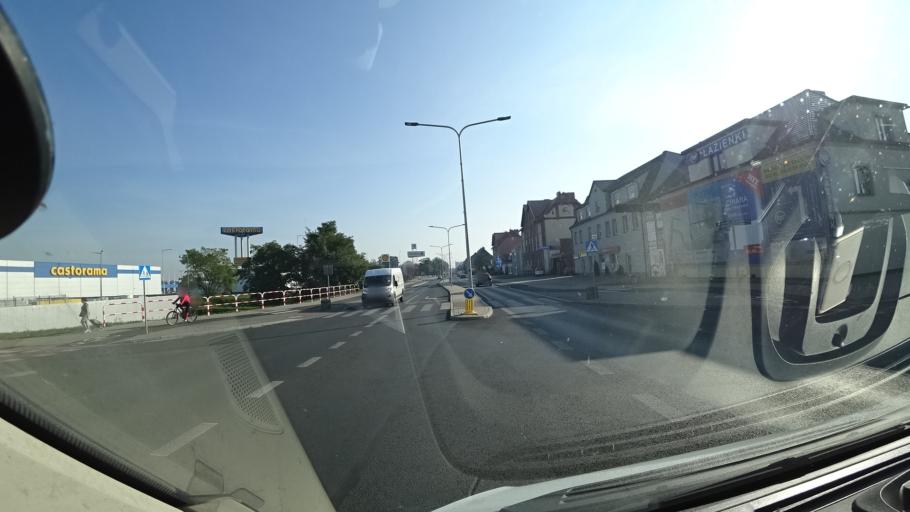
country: PL
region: Opole Voivodeship
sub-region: Powiat kedzierzynsko-kozielski
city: Kedzierzyn-Kozle
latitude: 50.3397
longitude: 18.1919
